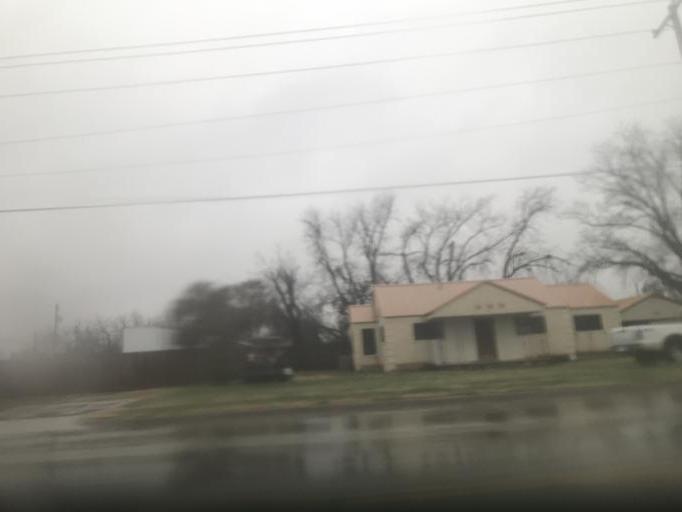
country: US
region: Texas
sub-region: Tom Green County
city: San Angelo
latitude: 31.4708
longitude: -100.4091
